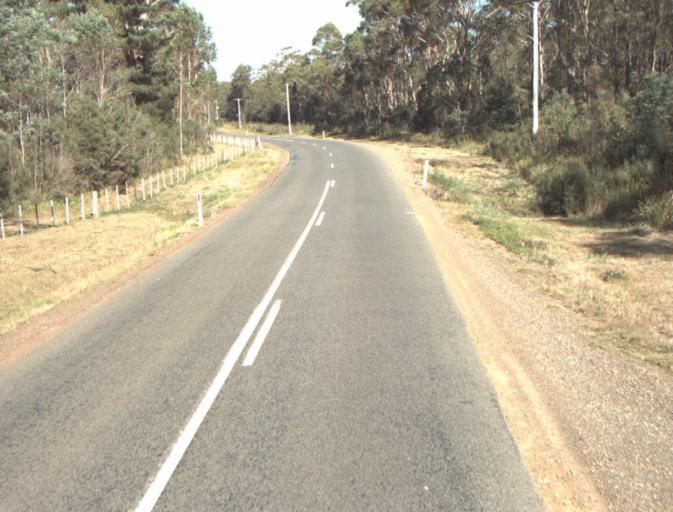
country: AU
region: Tasmania
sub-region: Launceston
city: Mayfield
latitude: -41.3328
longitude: 147.1409
